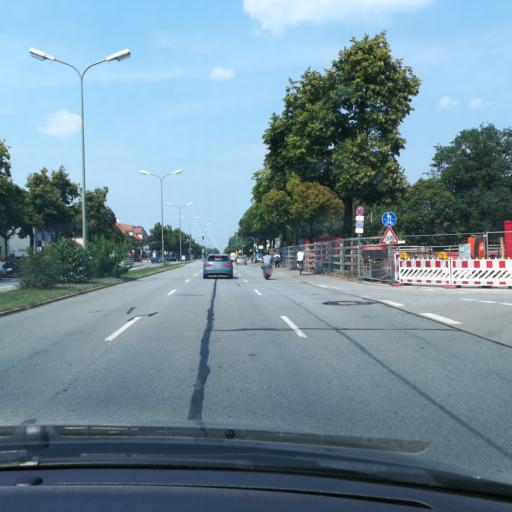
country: DE
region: Bavaria
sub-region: Upper Bavaria
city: Neuried
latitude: 48.1151
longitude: 11.5025
